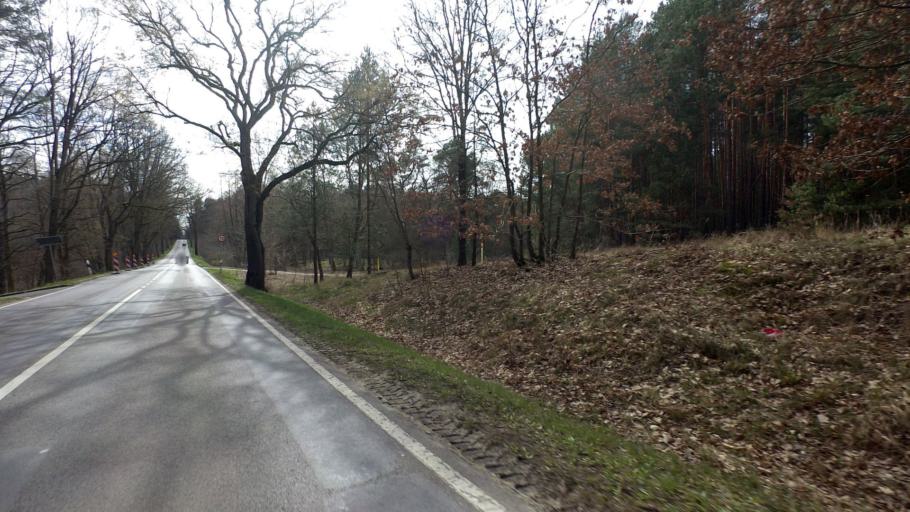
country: DE
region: Brandenburg
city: Birkenwerder
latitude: 52.7148
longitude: 13.3668
